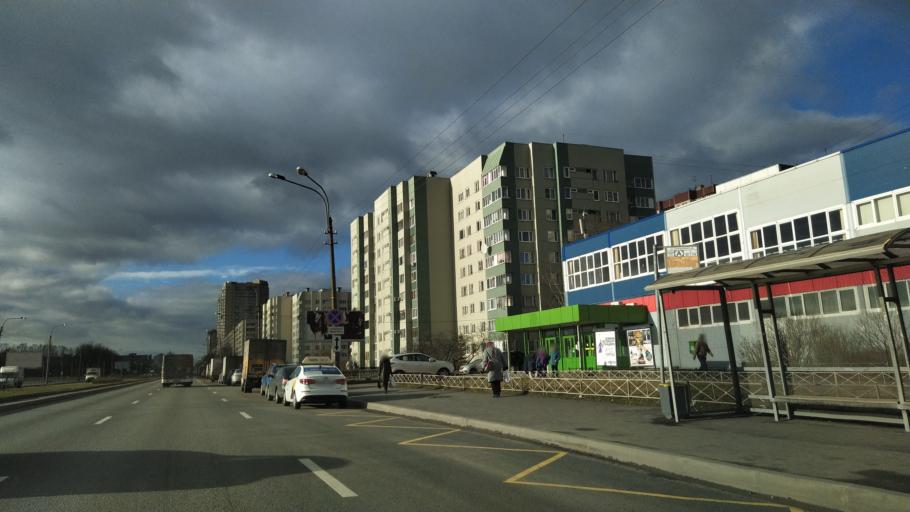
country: RU
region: St.-Petersburg
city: Grazhdanka
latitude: 60.0324
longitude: 30.3851
